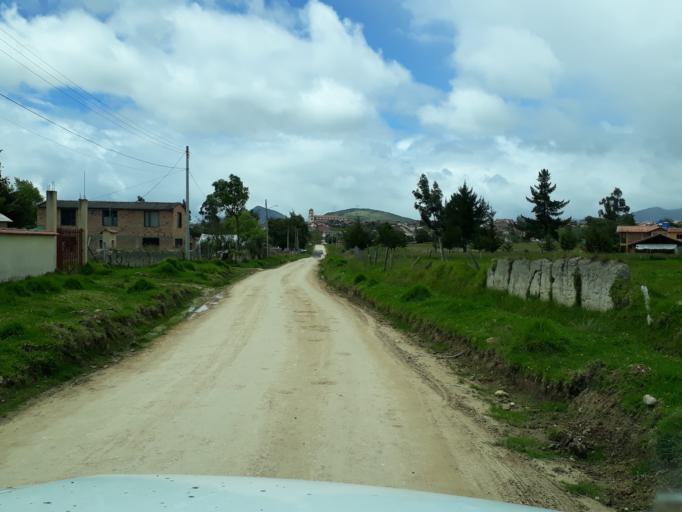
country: CO
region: Cundinamarca
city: Guasca
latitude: 4.8600
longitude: -73.8843
